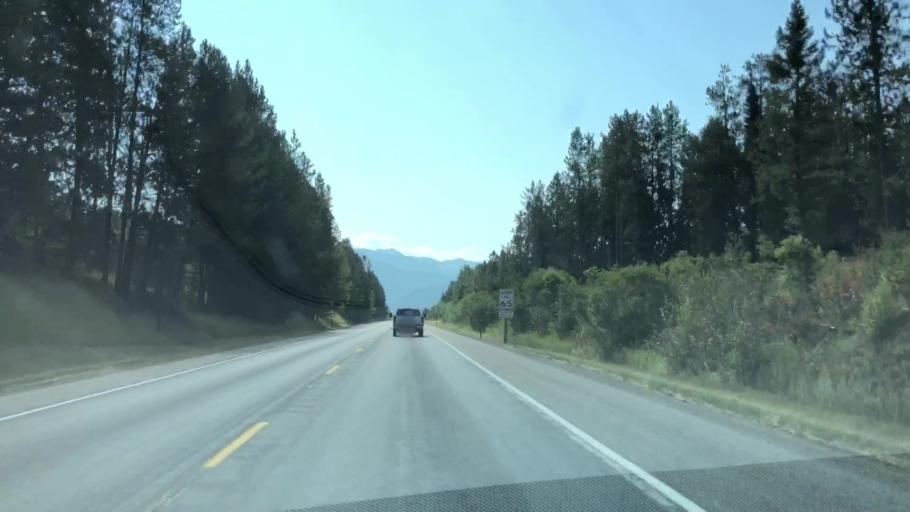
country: US
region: Wyoming
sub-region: Teton County
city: Hoback
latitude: 43.1995
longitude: -111.0429
